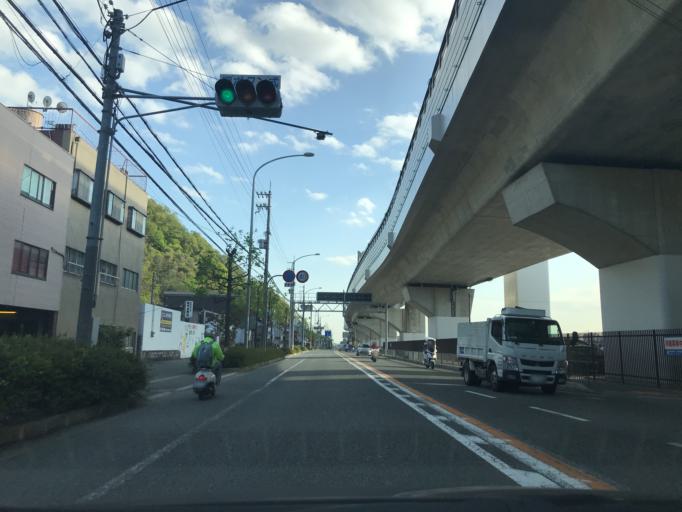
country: JP
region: Osaka
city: Ikeda
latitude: 34.8366
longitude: 135.4261
